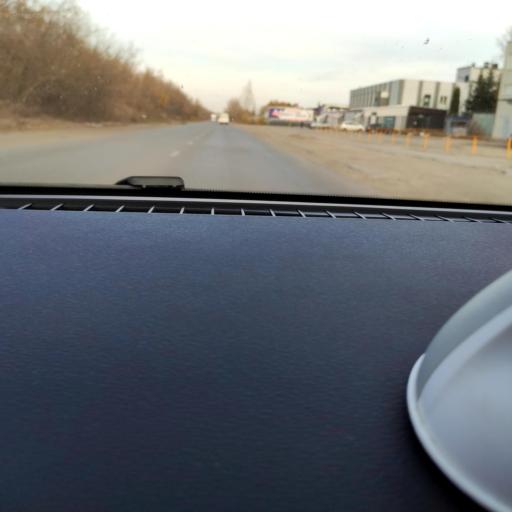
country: RU
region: Samara
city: Petra-Dubrava
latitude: 53.2548
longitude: 50.2788
